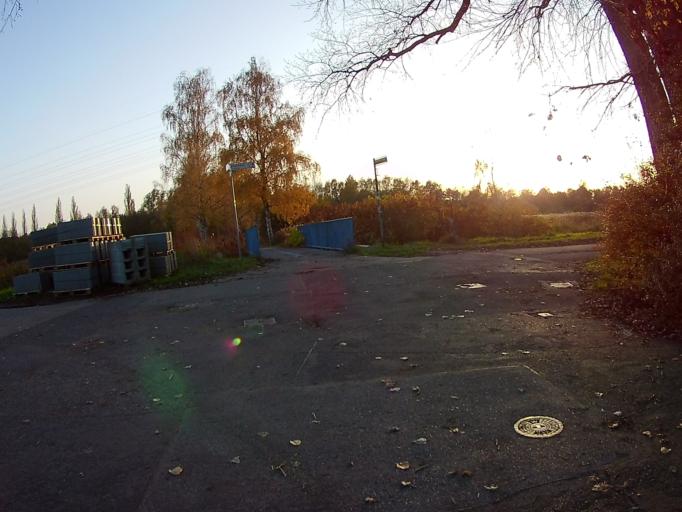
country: DE
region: Hamburg
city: Harburg
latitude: 53.4807
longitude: 9.9264
